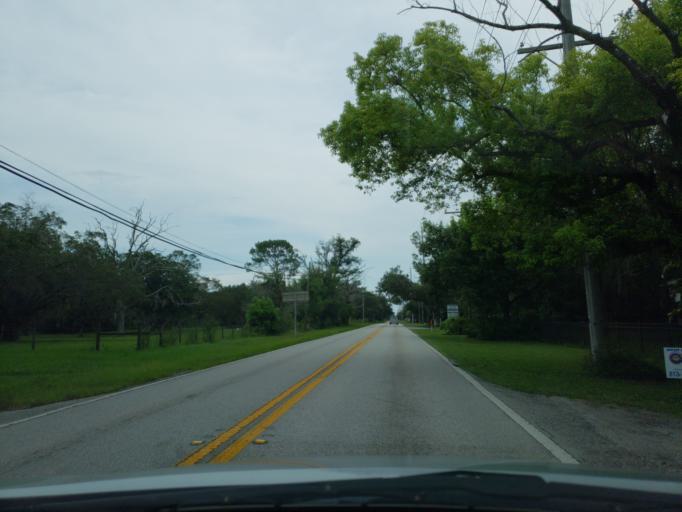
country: US
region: Florida
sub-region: Hillsborough County
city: Lutz
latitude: 28.1405
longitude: -82.4306
